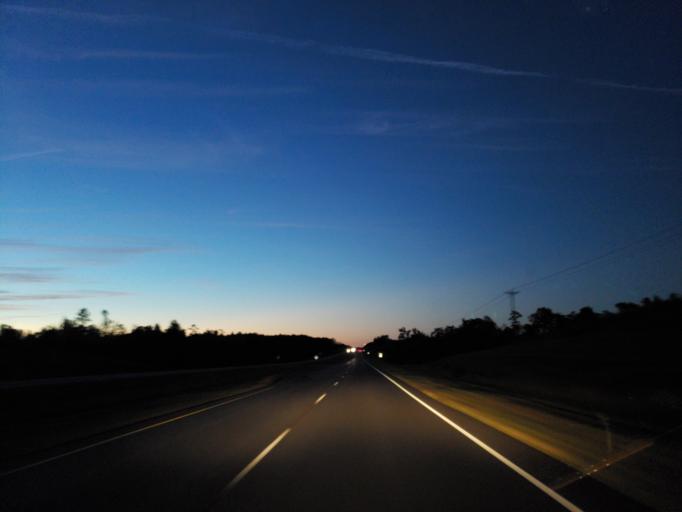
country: US
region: Mississippi
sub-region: Clarke County
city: Quitman
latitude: 32.0668
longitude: -88.6821
